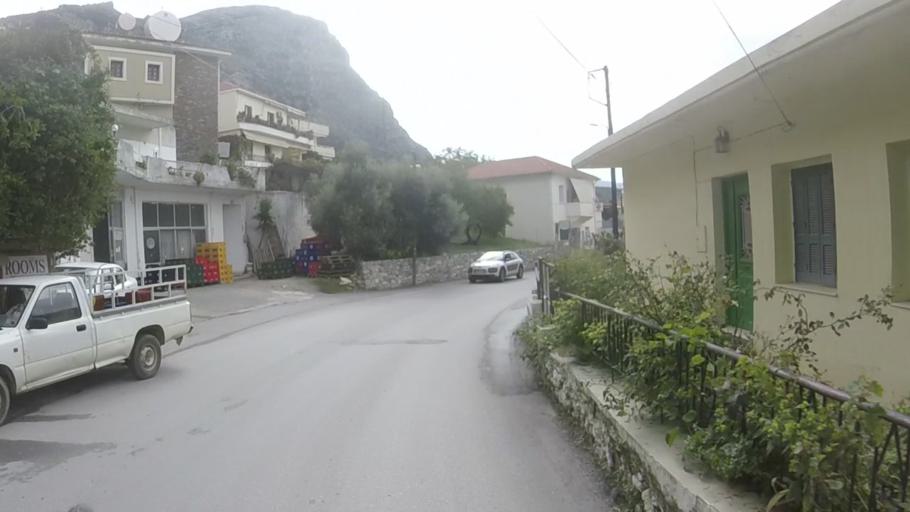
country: GR
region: Crete
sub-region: Nomos Rethymnis
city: Agia Foteini
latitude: 35.2197
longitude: 24.5339
